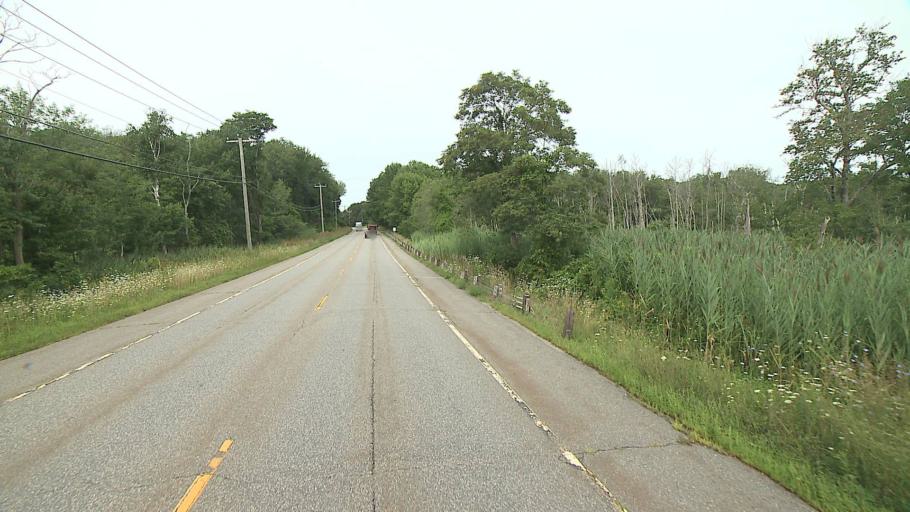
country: US
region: Connecticut
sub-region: Litchfield County
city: New Preston
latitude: 41.7439
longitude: -73.3642
